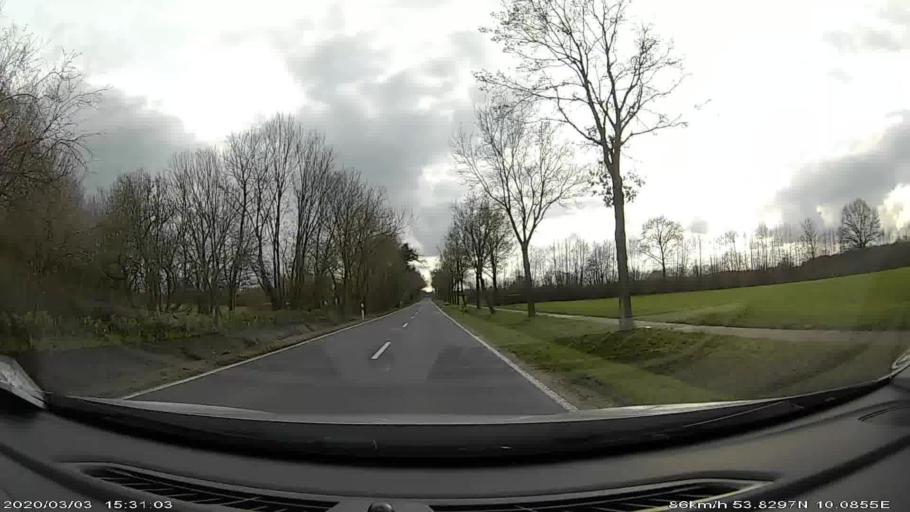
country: DE
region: Schleswig-Holstein
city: Huttblek
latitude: 53.8306
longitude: 10.0858
